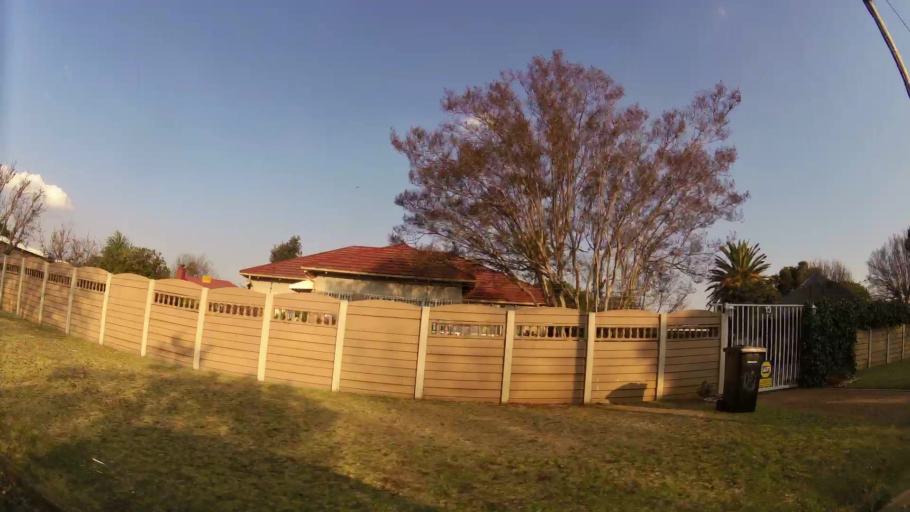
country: ZA
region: Gauteng
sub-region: Ekurhuleni Metropolitan Municipality
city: Springs
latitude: -26.2927
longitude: 28.4419
